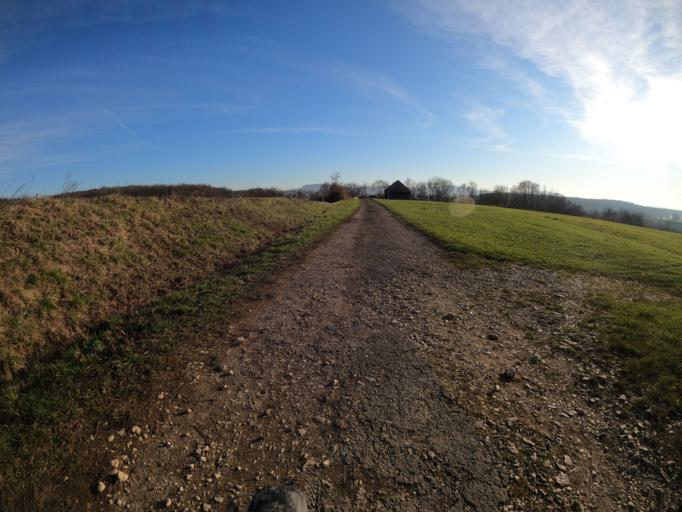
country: DE
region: Baden-Wuerttemberg
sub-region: Regierungsbezirk Stuttgart
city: Wangen
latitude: 48.7006
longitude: 9.6202
